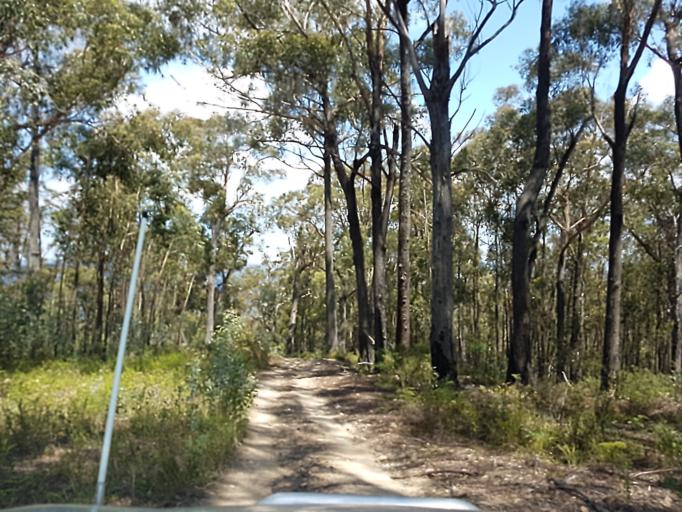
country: AU
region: Victoria
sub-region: East Gippsland
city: Lakes Entrance
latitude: -37.4004
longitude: 148.2983
